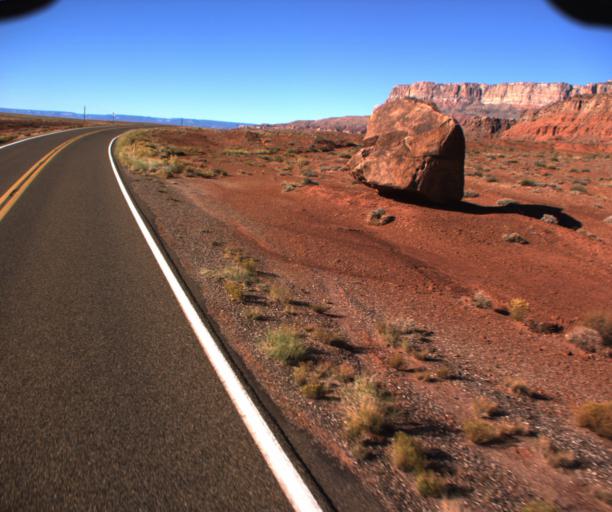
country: US
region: Arizona
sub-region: Coconino County
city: Page
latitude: 36.7546
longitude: -111.7178
